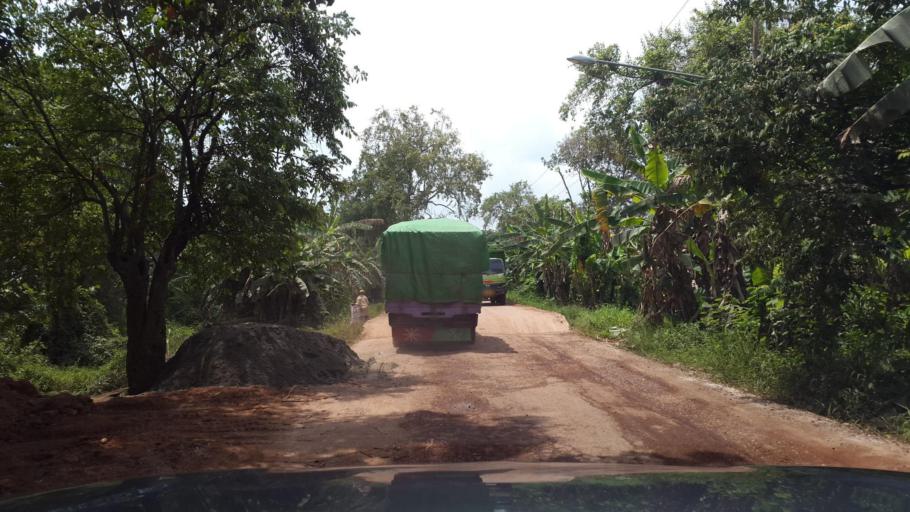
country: ID
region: South Sumatra
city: Tanjungraja
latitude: -3.1797
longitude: 104.8564
